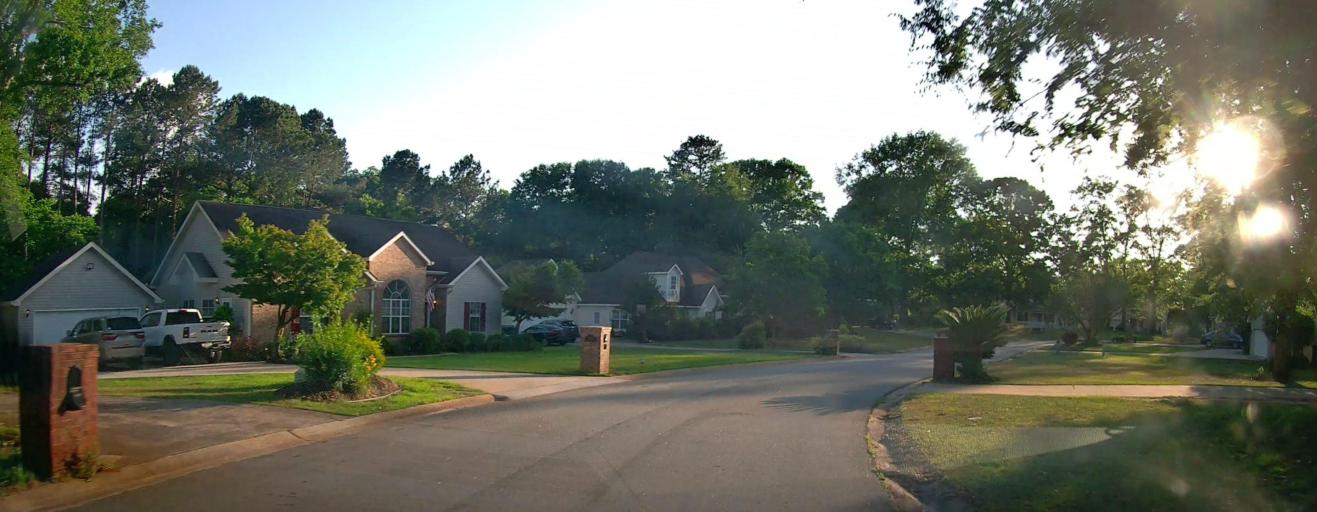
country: US
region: Georgia
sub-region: Houston County
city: Centerville
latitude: 32.6392
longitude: -83.7144
